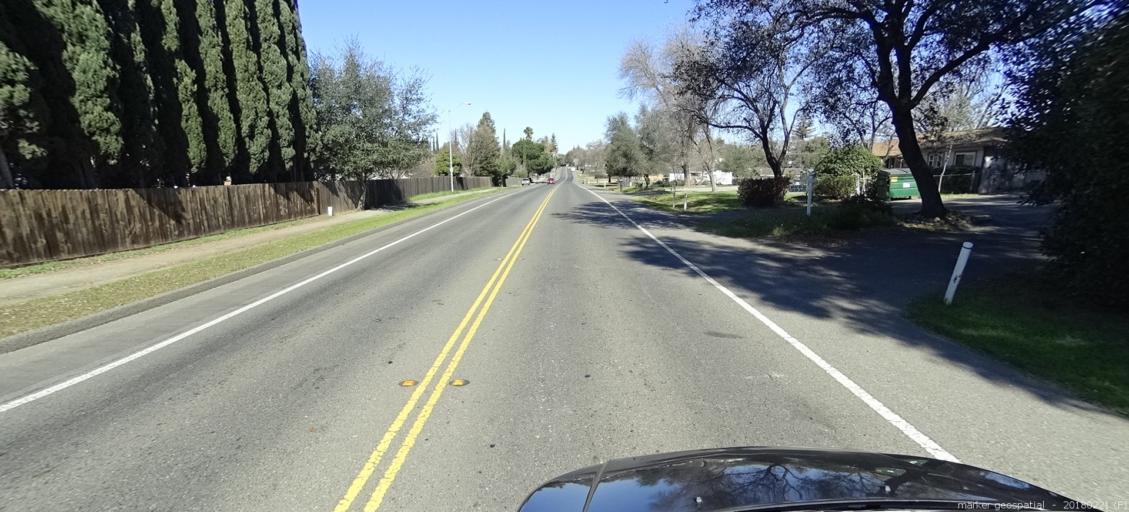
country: US
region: California
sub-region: Sacramento County
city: Citrus Heights
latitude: 38.7105
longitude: -121.2446
